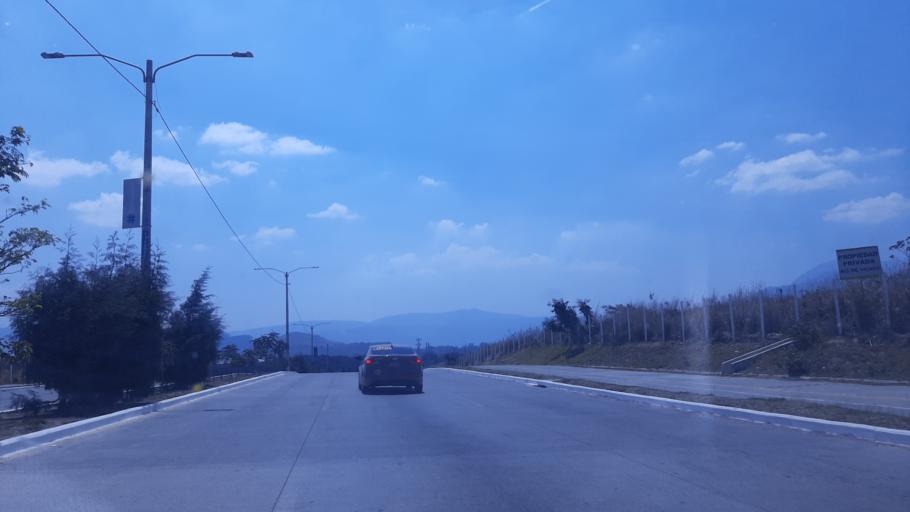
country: GT
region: Guatemala
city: Villa Nueva
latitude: 14.5135
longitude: -90.5890
